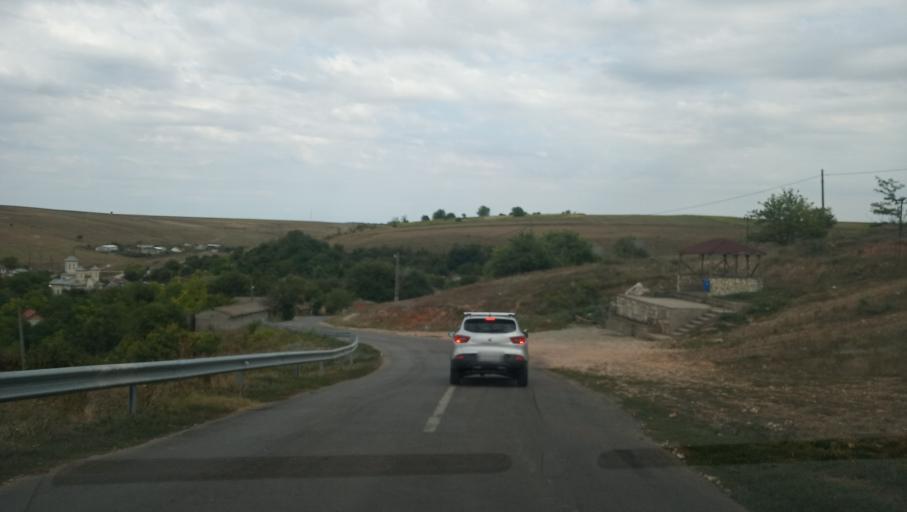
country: RO
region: Constanta
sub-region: Comuna Dumbraveni
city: Dumbraveni
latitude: 43.9895
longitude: 28.0075
